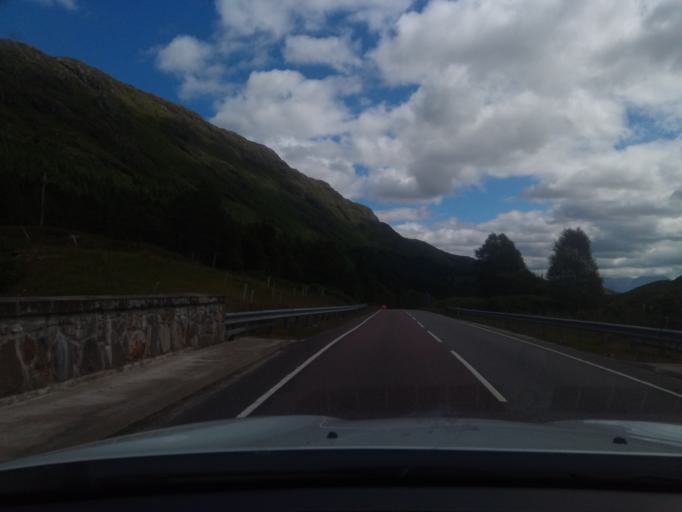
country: GB
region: Scotland
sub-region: Highland
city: Fort William
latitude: 56.8783
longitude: -5.4901
